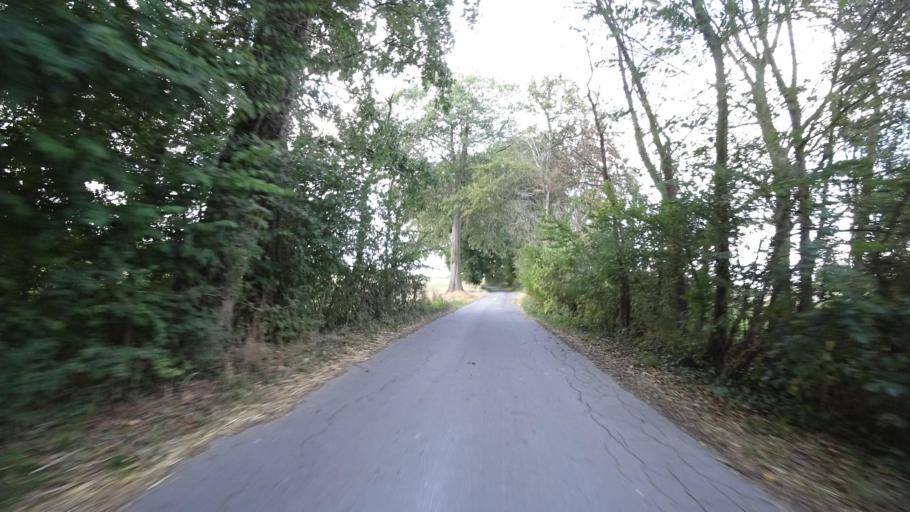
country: DE
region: North Rhine-Westphalia
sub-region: Regierungsbezirk Detmold
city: Rheda-Wiedenbruck
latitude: 51.8336
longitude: 8.2743
